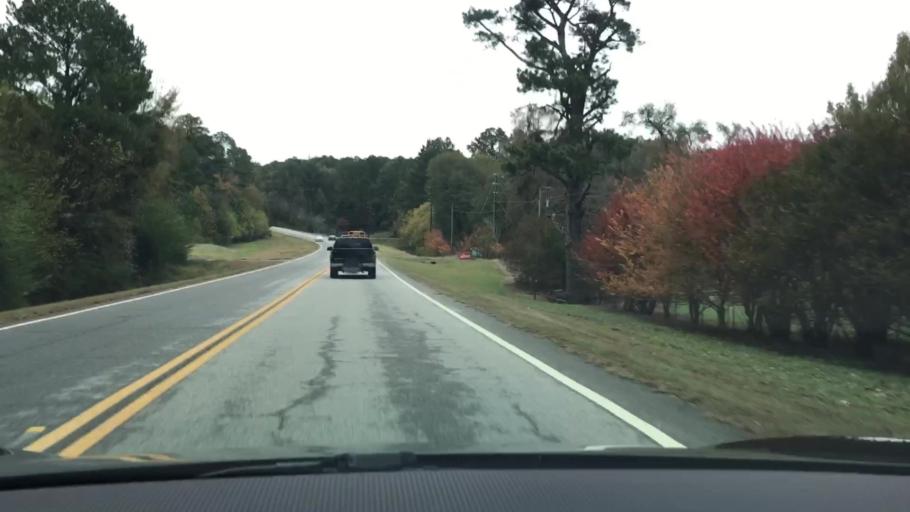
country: US
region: Georgia
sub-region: Greene County
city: Greensboro
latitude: 33.6429
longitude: -83.2290
